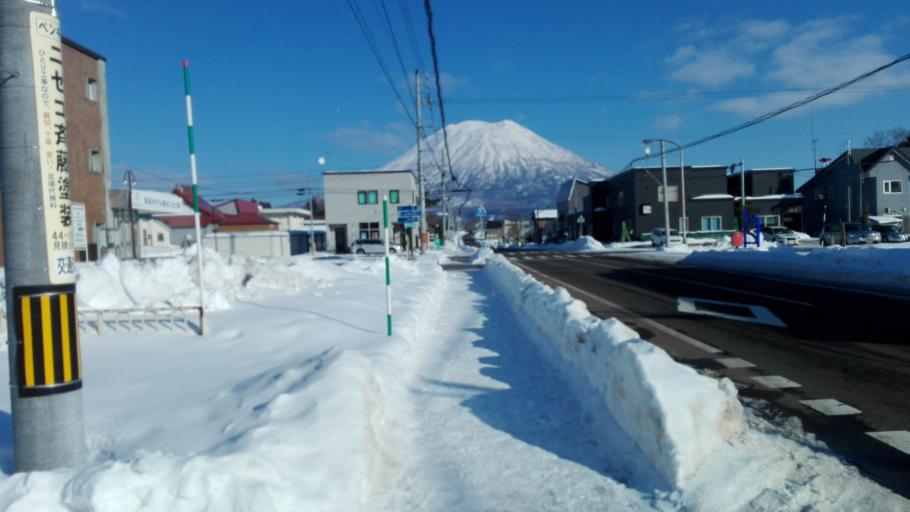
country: JP
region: Hokkaido
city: Niseko Town
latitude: 42.8043
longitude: 140.6871
